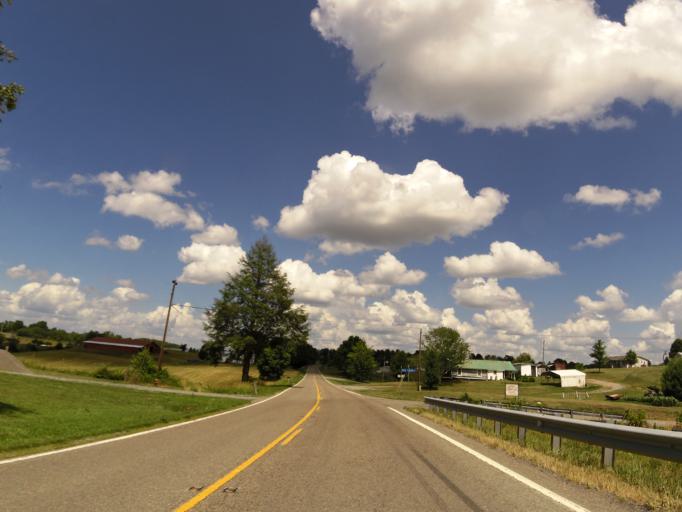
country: US
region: Virginia
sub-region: Lee County
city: Jonesville
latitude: 36.6956
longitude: -83.0495
